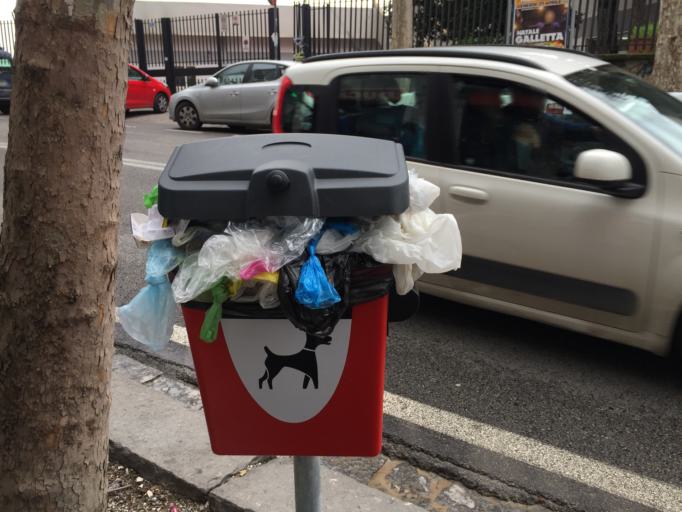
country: IT
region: Campania
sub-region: Provincia di Napoli
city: Napoli
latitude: 40.8593
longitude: 14.2309
